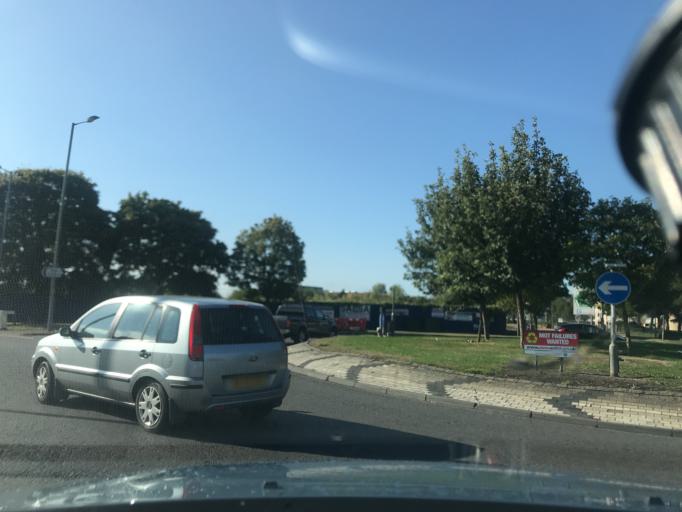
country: GB
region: England
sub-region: Buckinghamshire
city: Aylesbury
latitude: 51.8231
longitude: -0.8254
